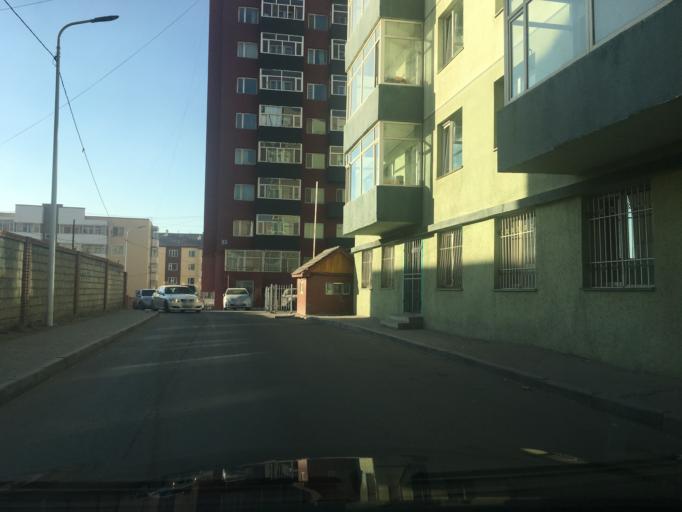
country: MN
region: Ulaanbaatar
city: Ulaanbaatar
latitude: 47.9172
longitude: 106.8735
